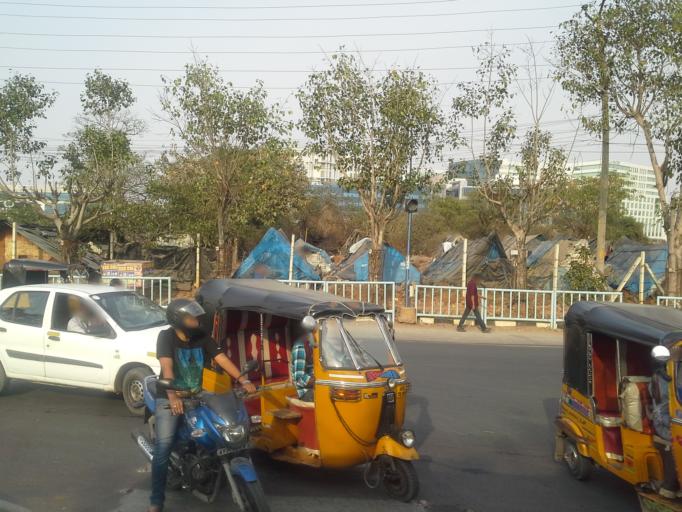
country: IN
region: Telangana
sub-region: Medak
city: Serilingampalle
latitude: 17.4451
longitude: 78.3526
